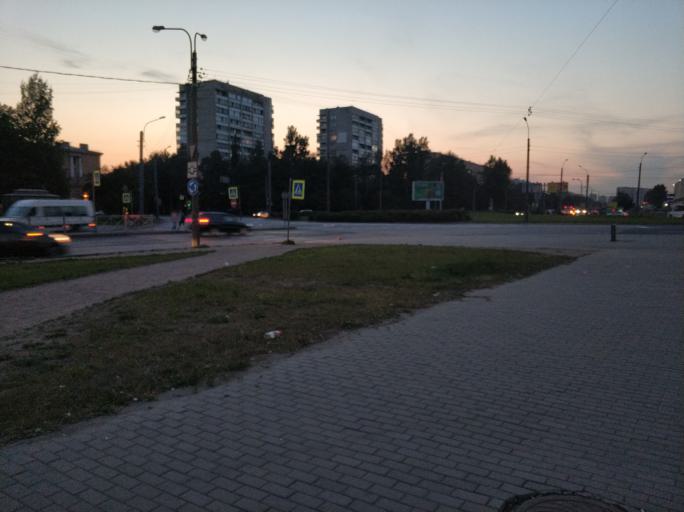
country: RU
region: St.-Petersburg
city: Krasnogvargeisky
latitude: 59.9593
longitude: 30.4387
